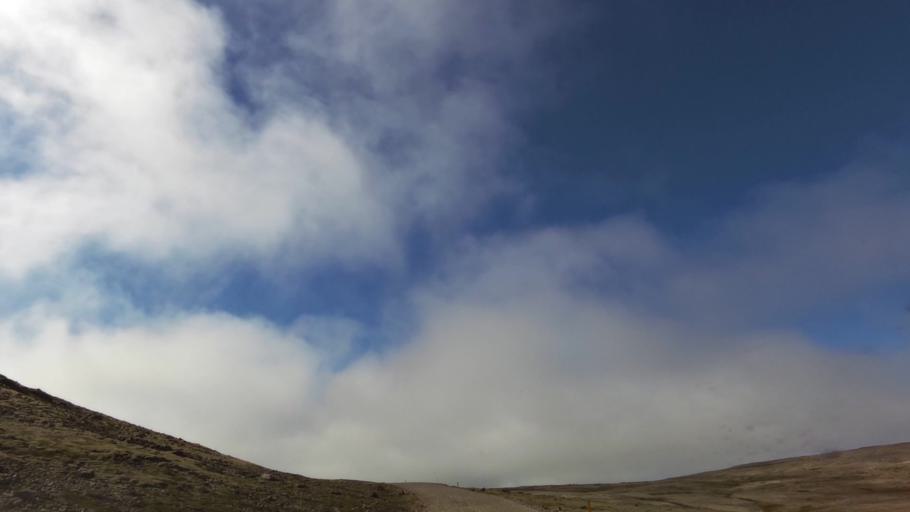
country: IS
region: West
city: Olafsvik
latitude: 65.5535
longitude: -24.2286
